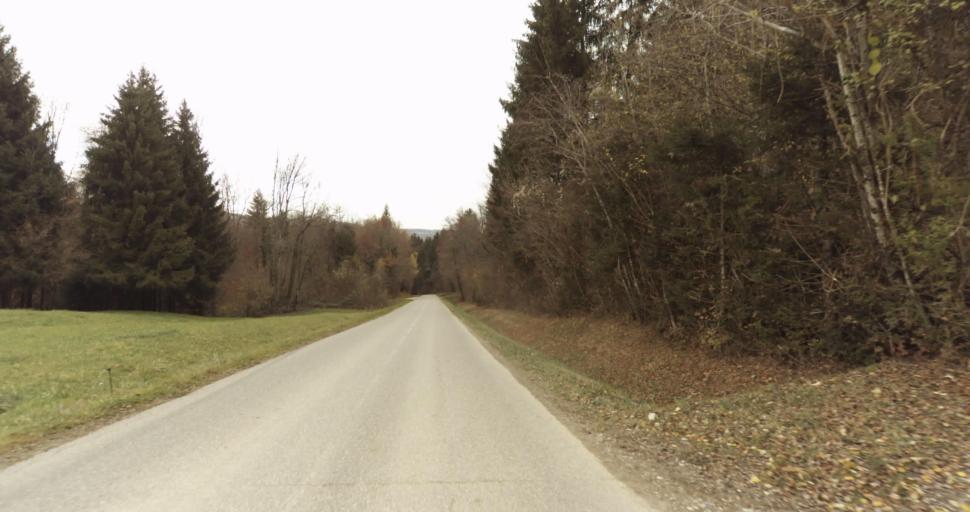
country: FR
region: Rhone-Alpes
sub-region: Departement de la Haute-Savoie
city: Groisy
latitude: 45.9956
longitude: 6.1820
